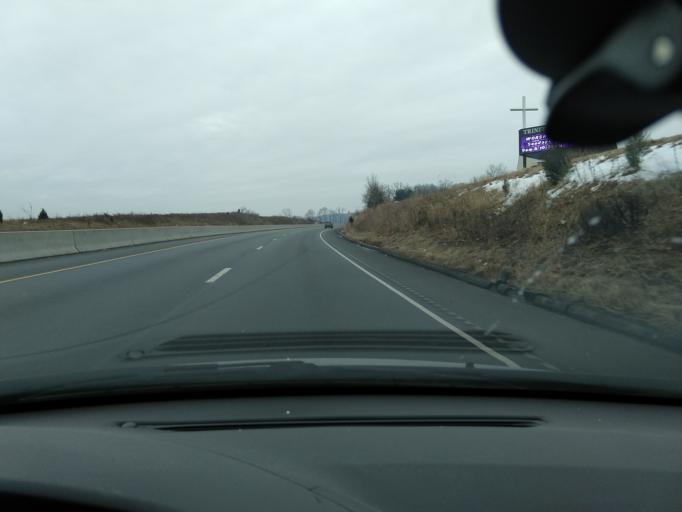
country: US
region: Pennsylvania
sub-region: Montgomery County
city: Gilbertsville
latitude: 40.3224
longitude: -75.6240
